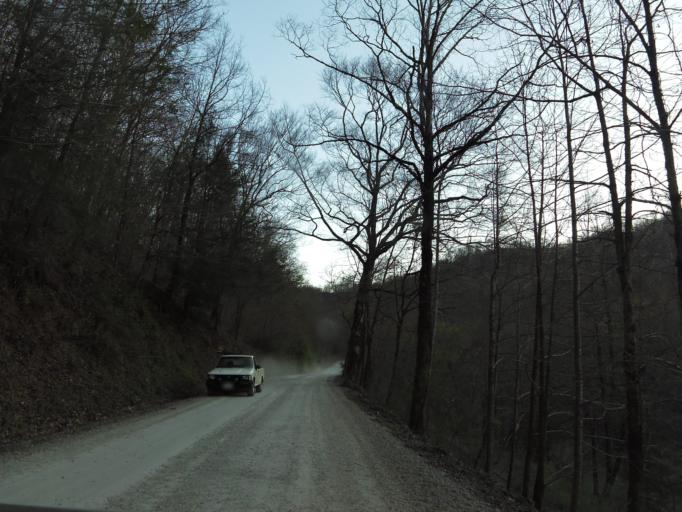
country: US
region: Tennessee
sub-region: Campbell County
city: Caryville
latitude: 36.2163
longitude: -84.3259
